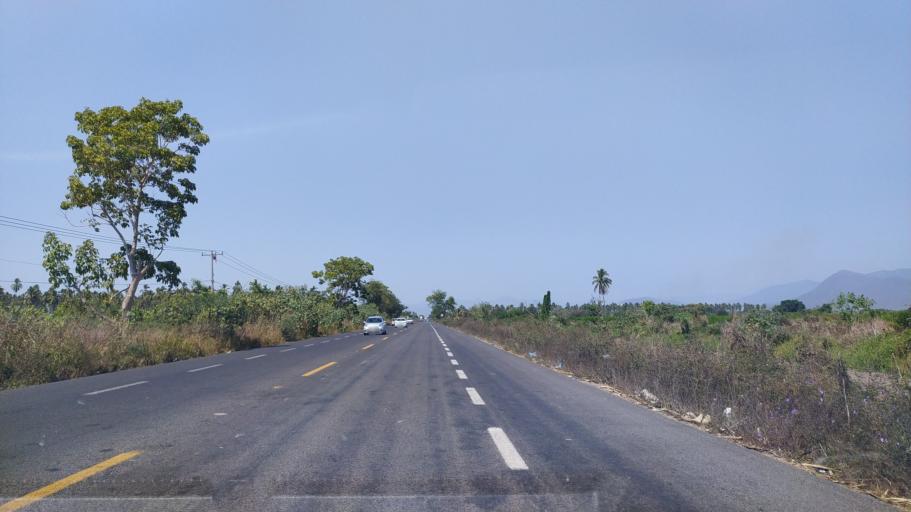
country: MX
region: Colima
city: Tecoman
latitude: 18.8324
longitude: -103.8177
